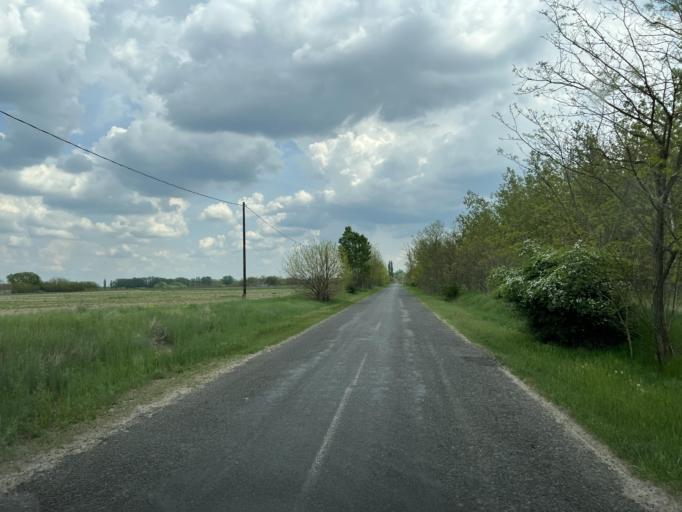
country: HU
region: Pest
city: Nagykoros
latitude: 47.0919
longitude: 19.7635
